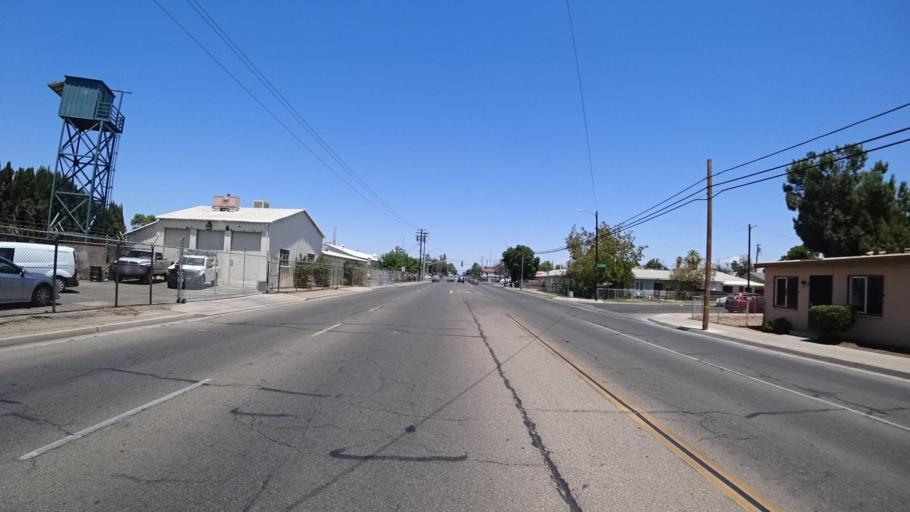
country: US
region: California
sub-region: Fresno County
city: Fresno
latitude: 36.7348
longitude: -119.7455
